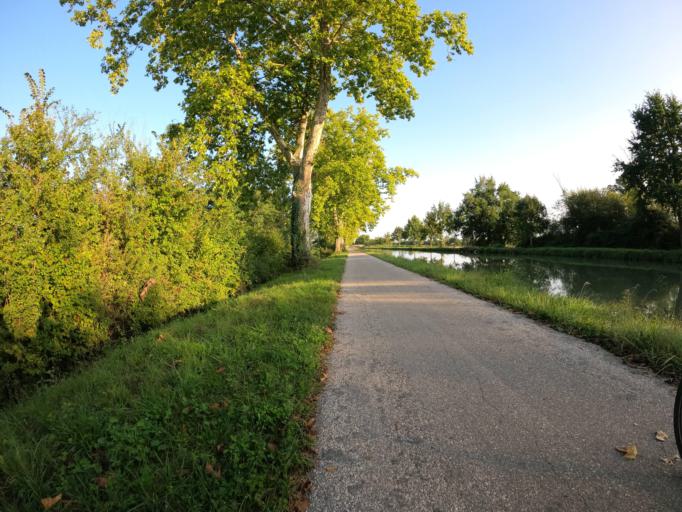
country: FR
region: Midi-Pyrenees
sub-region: Departement du Tarn-et-Garonne
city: Saint-Porquier
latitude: 44.0183
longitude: 1.1694
